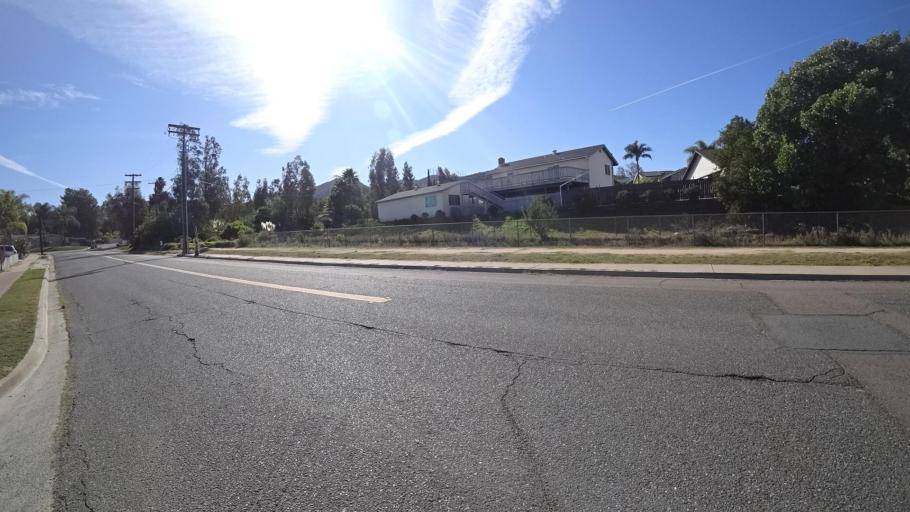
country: US
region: California
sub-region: San Diego County
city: Granite Hills
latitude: 32.8324
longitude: -116.8994
